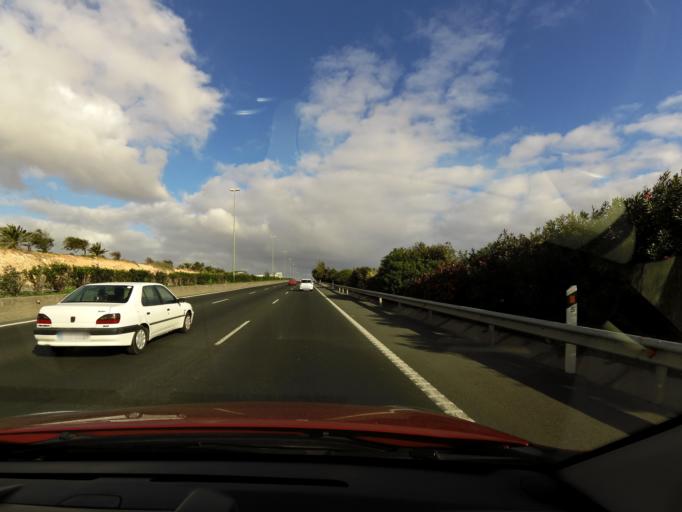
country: ES
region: Canary Islands
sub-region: Provincia de Las Palmas
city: Telde
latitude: 27.9559
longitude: -15.3876
